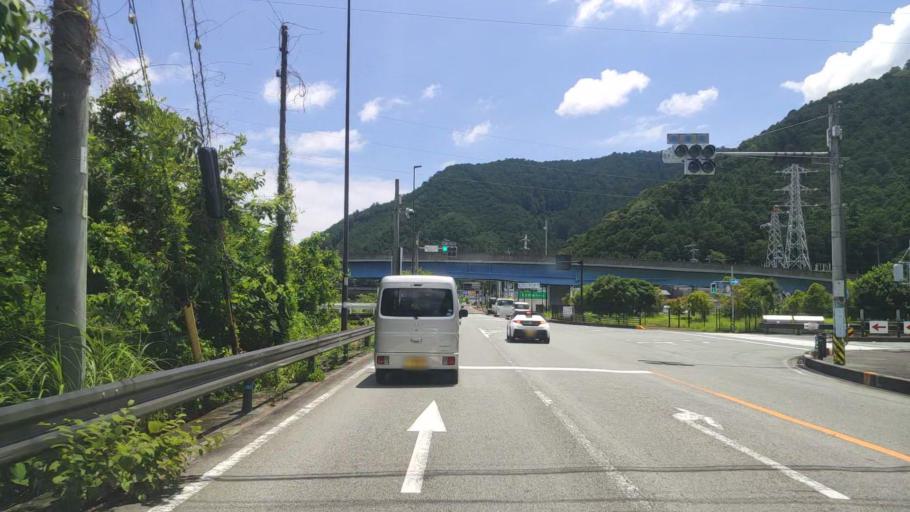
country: JP
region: Mie
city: Owase
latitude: 34.1200
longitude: 136.2191
